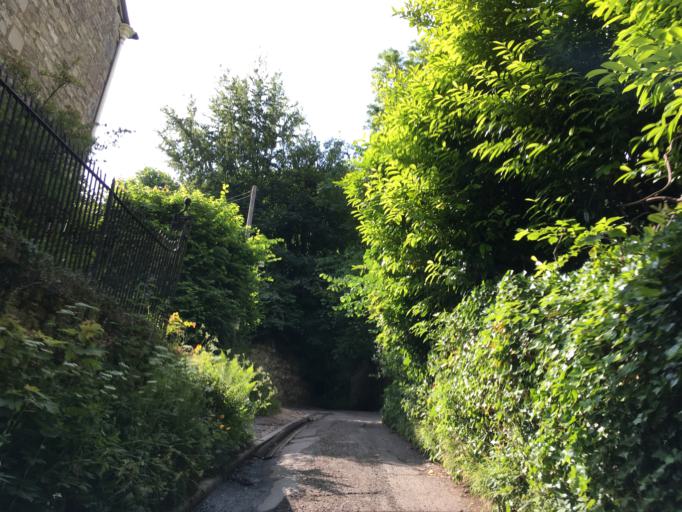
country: GB
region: England
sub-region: Gloucestershire
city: Brimscombe
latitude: 51.7160
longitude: -2.1796
